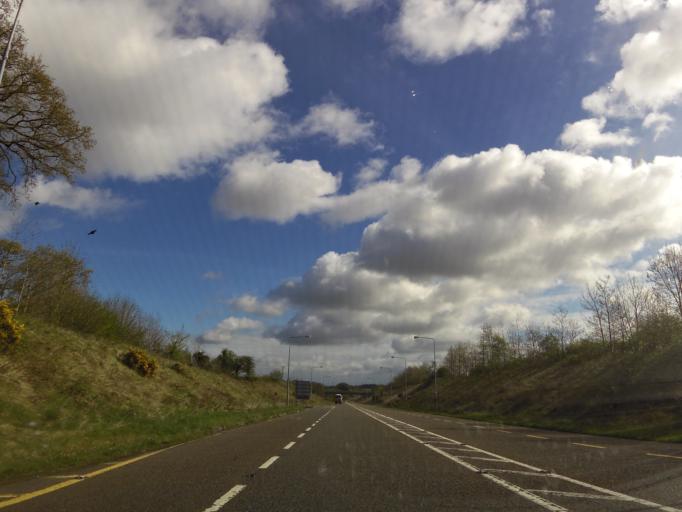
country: IE
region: Connaught
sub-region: Maigh Eo
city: Kiltamagh
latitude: 53.7951
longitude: -8.9273
